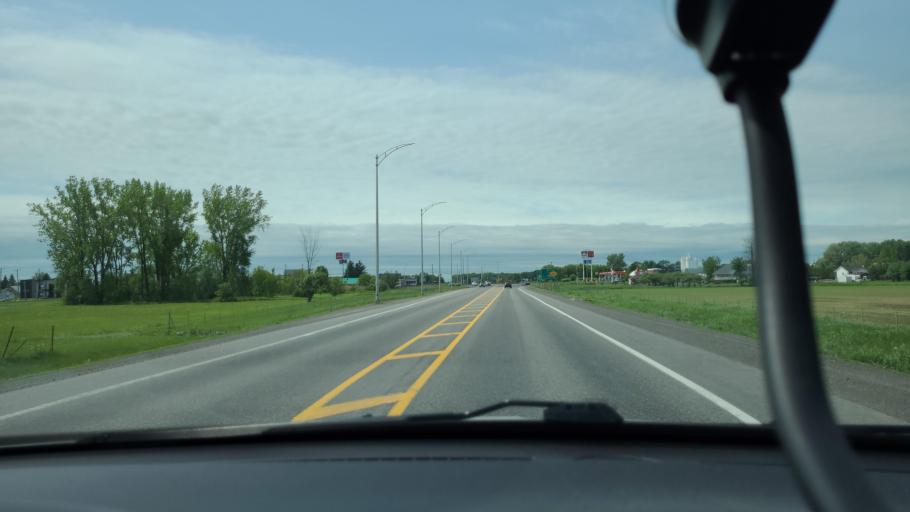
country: CA
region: Quebec
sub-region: Lanaudiere
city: Saint-Jacques
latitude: 45.9554
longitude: -73.5754
